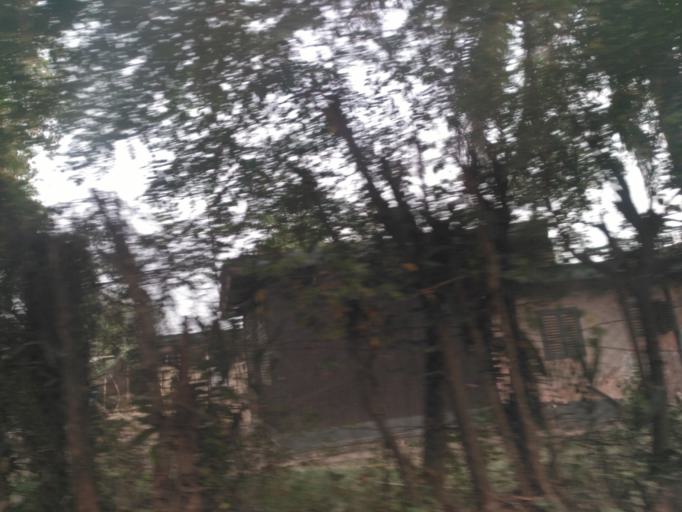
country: GH
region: Ashanti
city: Kumasi
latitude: 6.6660
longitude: -1.6144
